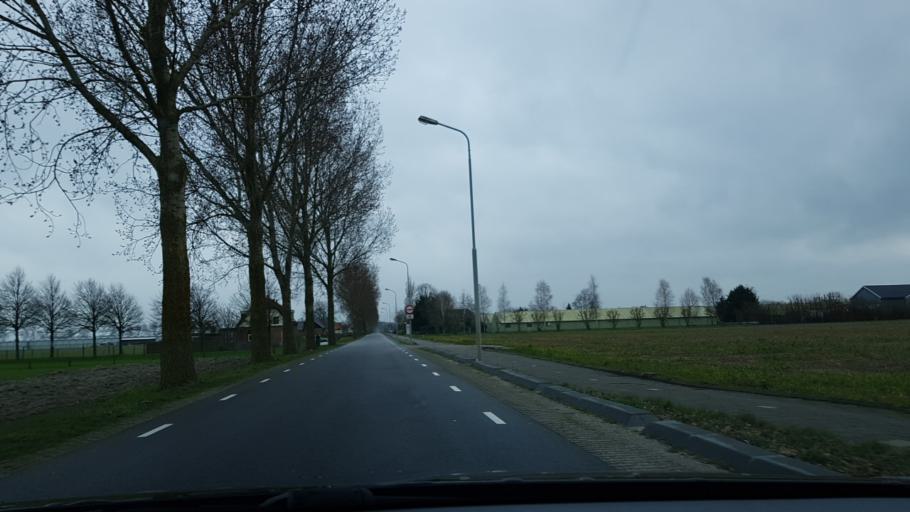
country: NL
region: South Holland
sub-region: Gemeente Kaag en Braassem
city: Leimuiden
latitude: 52.2597
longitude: 4.6674
